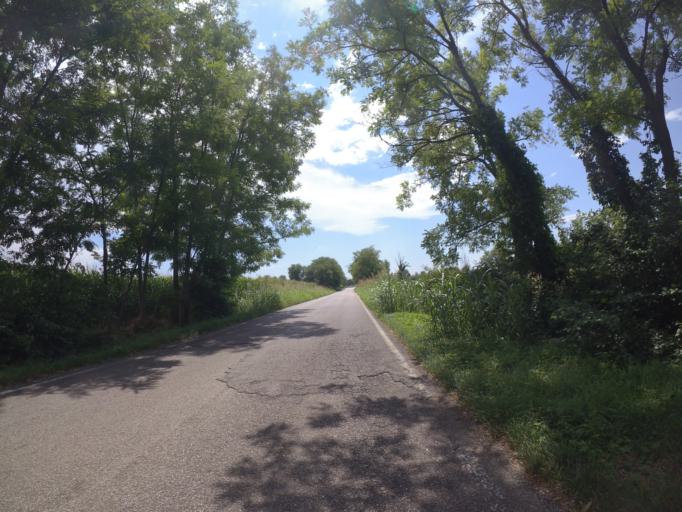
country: IT
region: Friuli Venezia Giulia
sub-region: Provincia di Udine
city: Talmassons
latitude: 45.9447
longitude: 13.0964
